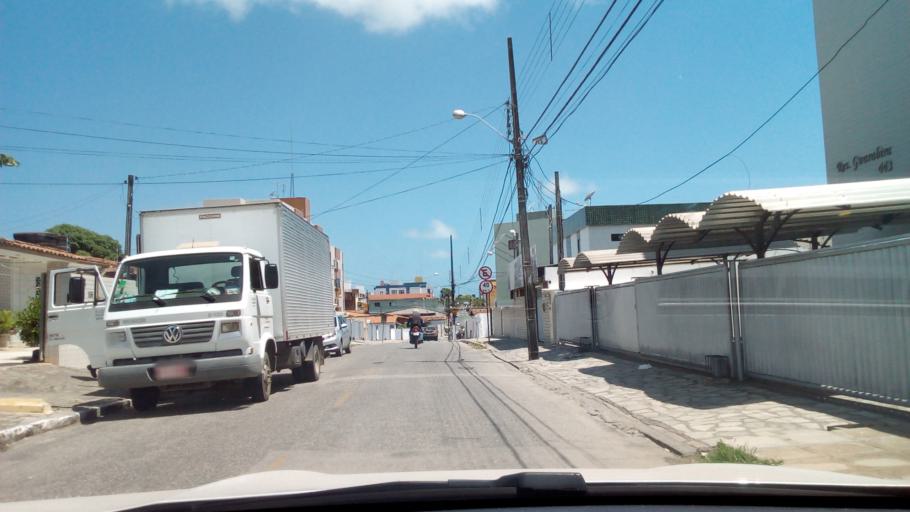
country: BR
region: Paraiba
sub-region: Joao Pessoa
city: Joao Pessoa
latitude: -7.1513
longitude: -34.8475
